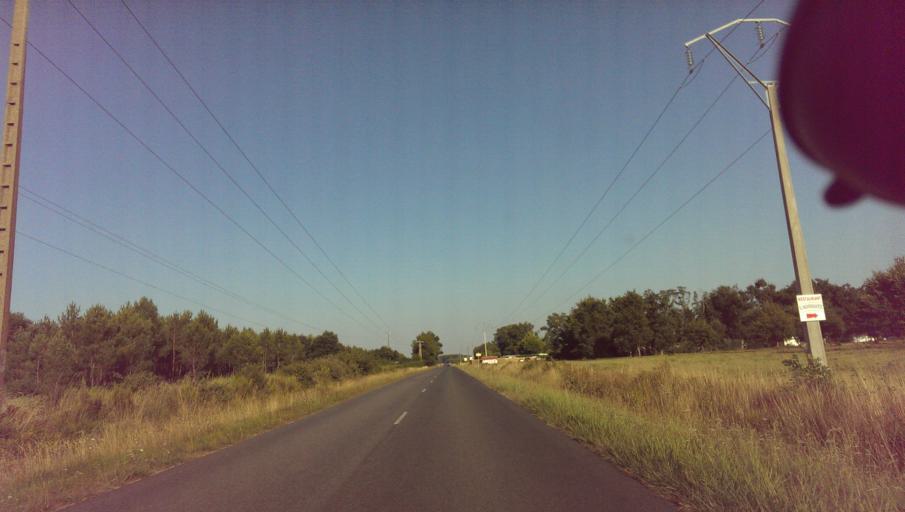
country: FR
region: Aquitaine
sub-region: Departement des Landes
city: Mimizan
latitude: 44.1831
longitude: -1.1845
